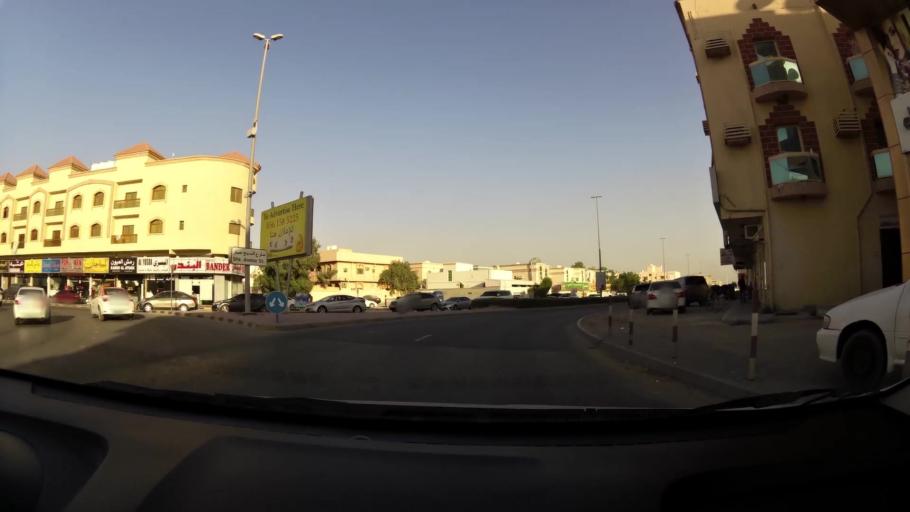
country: AE
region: Ajman
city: Ajman
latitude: 25.3933
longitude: 55.5051
